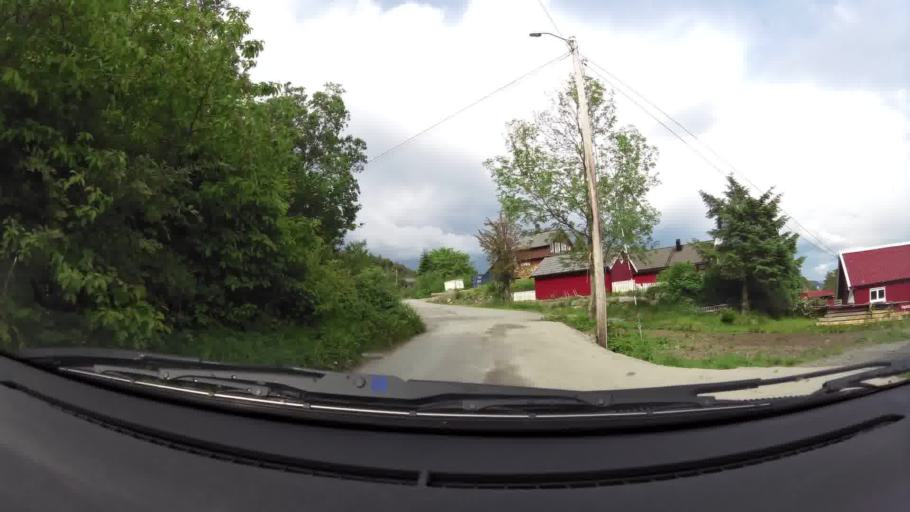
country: NO
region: More og Romsdal
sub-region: Kristiansund
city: Kristiansund
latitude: 63.0279
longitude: 7.7494
